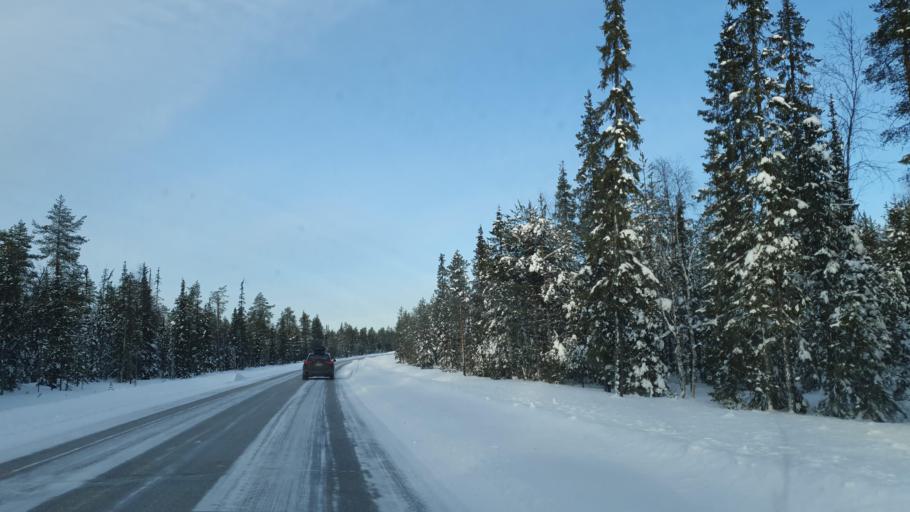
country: FI
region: Lapland
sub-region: Tunturi-Lappi
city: Kolari
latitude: 67.4843
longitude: 23.8780
